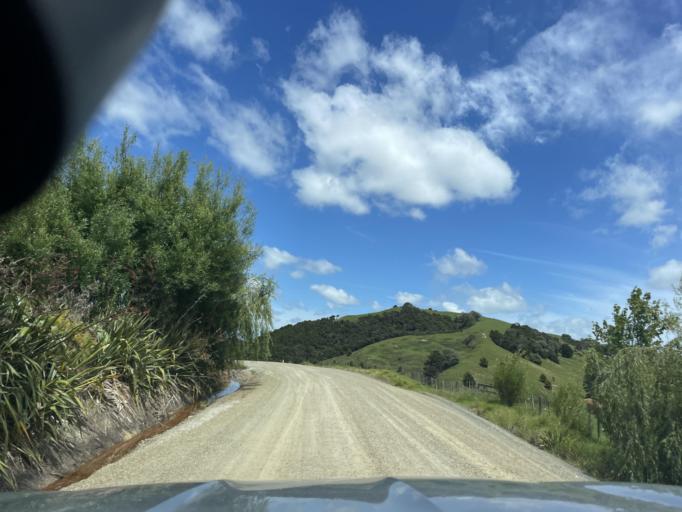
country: NZ
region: Auckland
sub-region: Auckland
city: Wellsford
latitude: -36.1626
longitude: 174.2844
